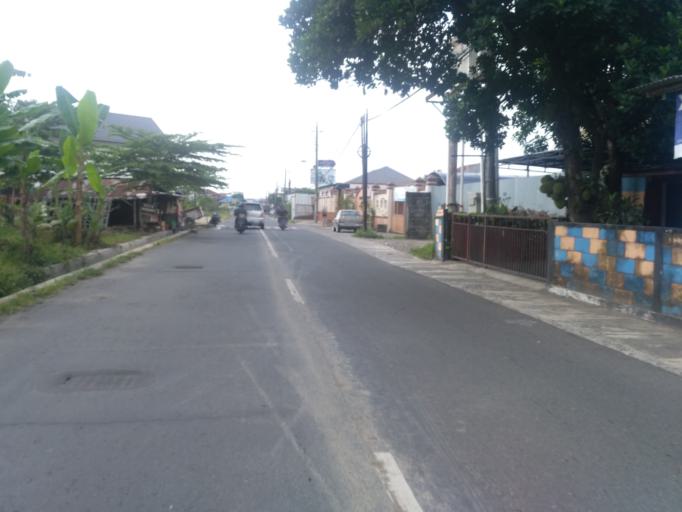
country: ID
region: Daerah Istimewa Yogyakarta
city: Yogyakarta
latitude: -7.7700
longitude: 110.3573
